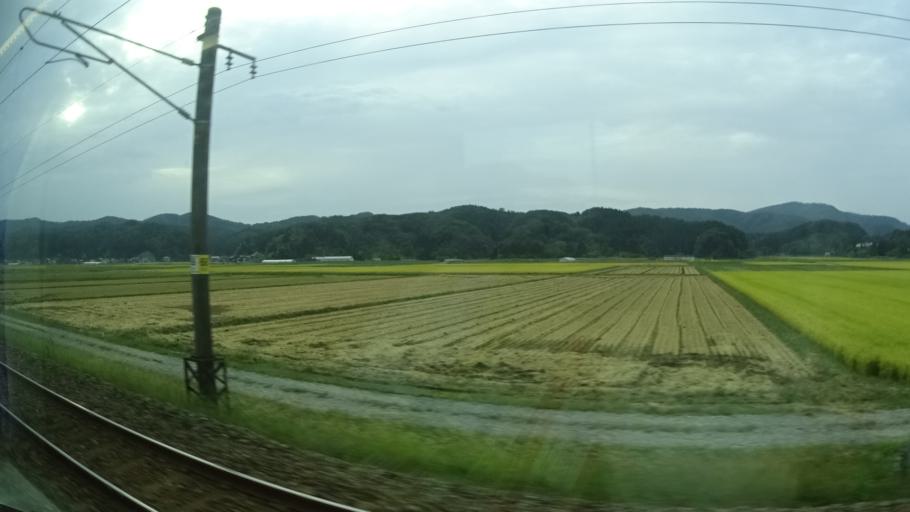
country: JP
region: Yamagata
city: Tsuruoka
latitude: 38.7106
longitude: 139.7266
